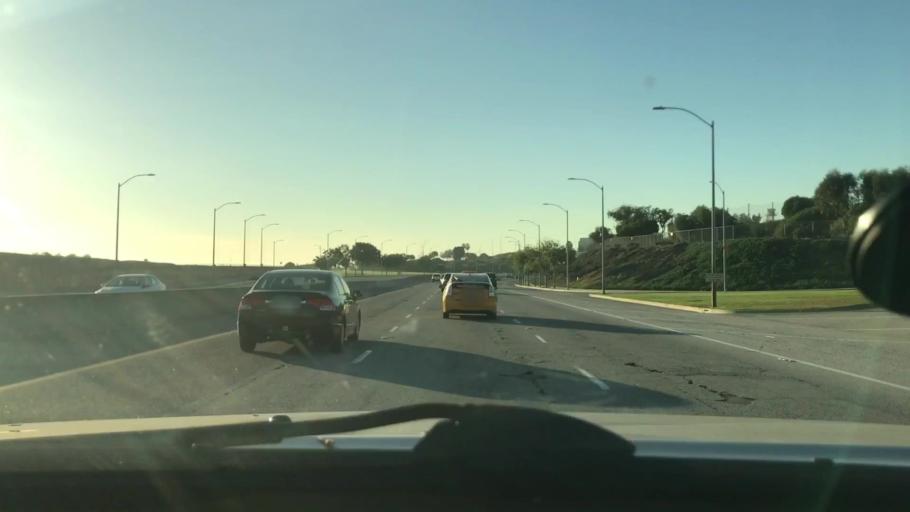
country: US
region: California
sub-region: Los Angeles County
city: El Segundo
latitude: 33.9534
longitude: -118.4080
